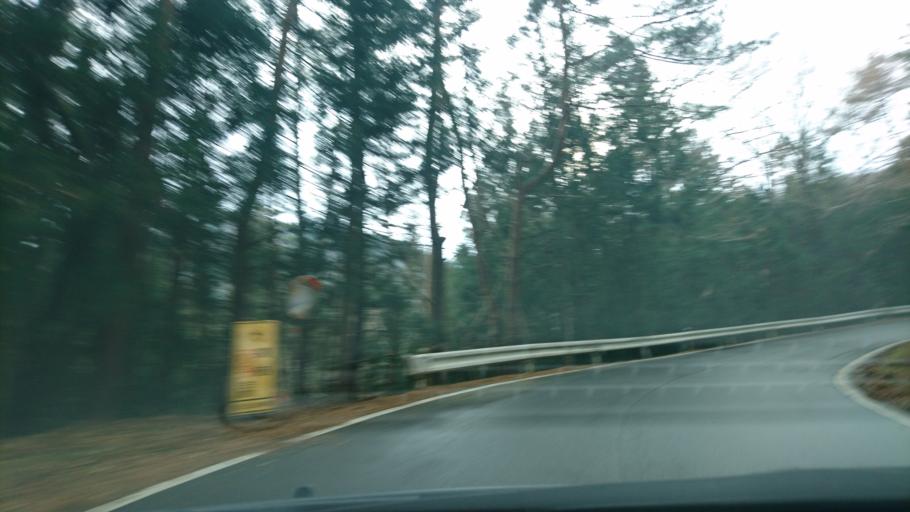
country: JP
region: Iwate
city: Ofunato
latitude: 38.9923
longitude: 141.5493
